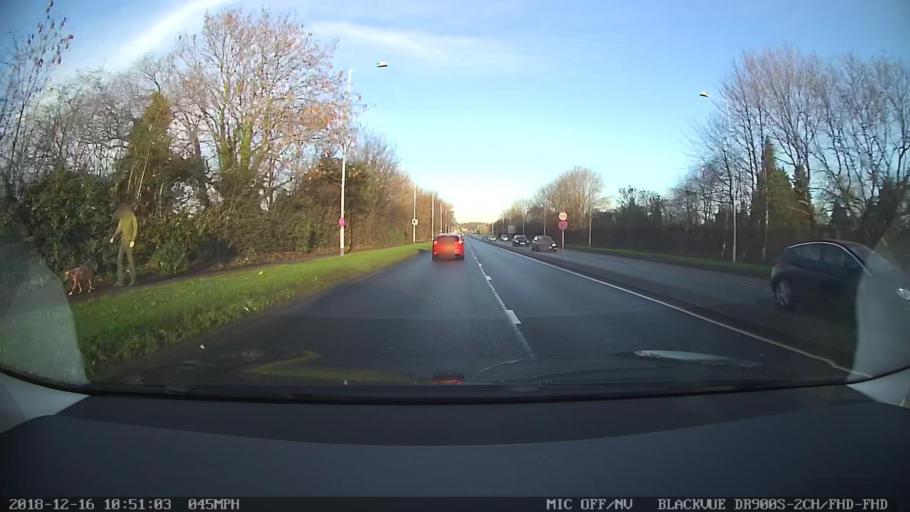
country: GB
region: England
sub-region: Manchester
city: Didsbury
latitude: 53.3849
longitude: -2.2233
